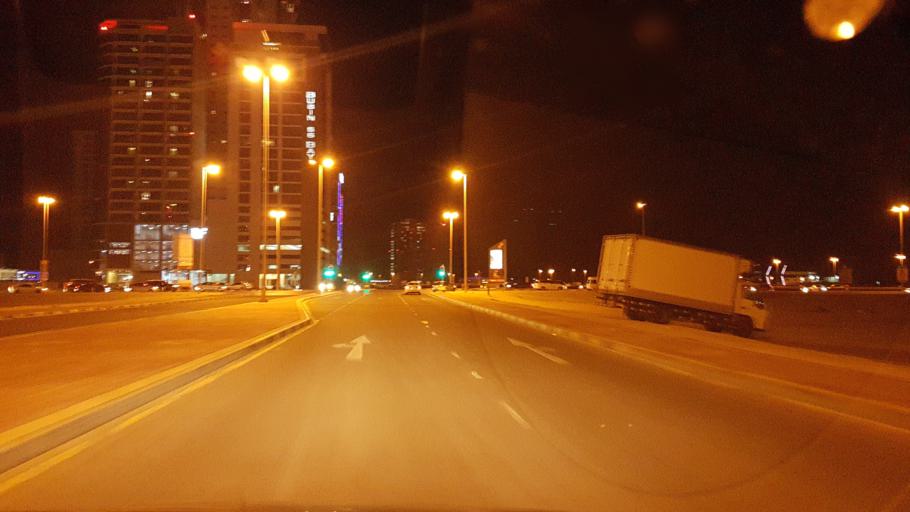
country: BH
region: Manama
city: Jidd Hafs
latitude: 26.2340
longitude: 50.5573
